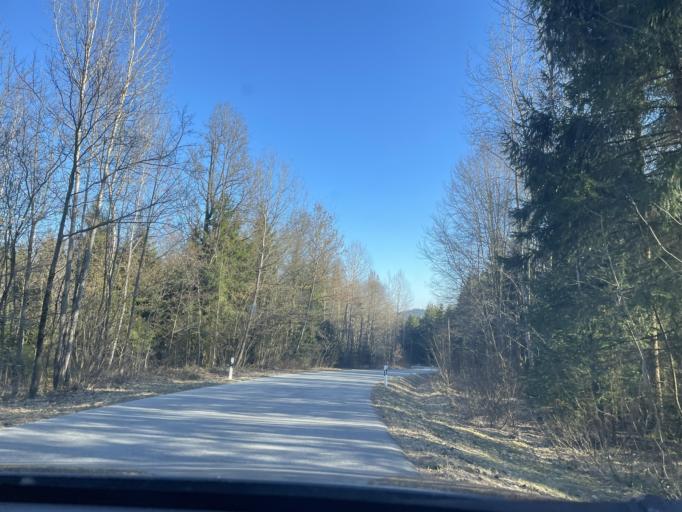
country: DE
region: Bavaria
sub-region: Lower Bavaria
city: Geiersthal
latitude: 49.0777
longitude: 12.9746
